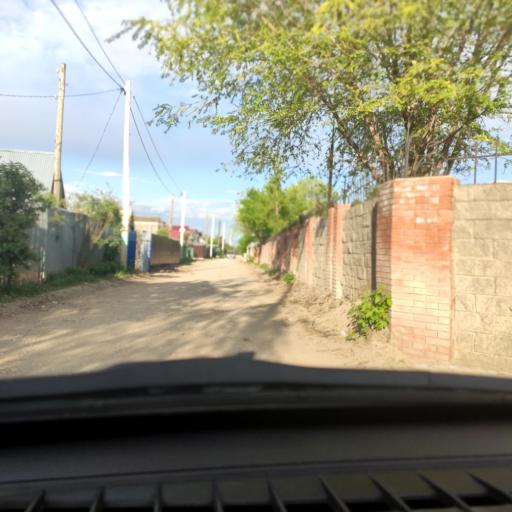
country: RU
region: Samara
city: Zhigulevsk
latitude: 53.4488
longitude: 49.5421
